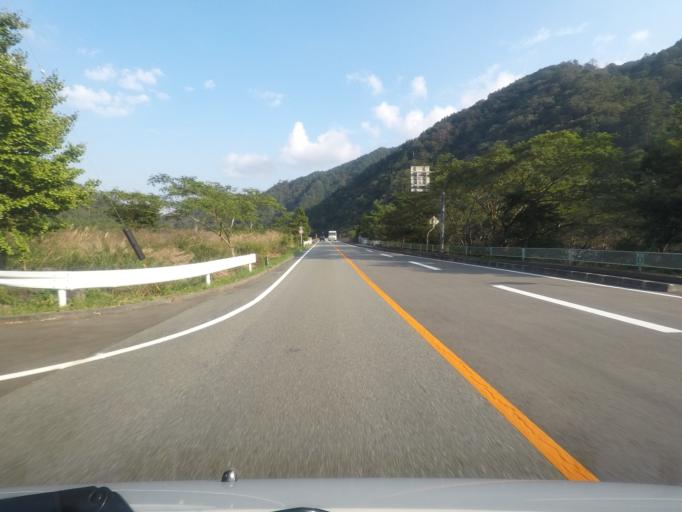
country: JP
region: Fukushima
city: Namie
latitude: 37.5107
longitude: 140.8938
